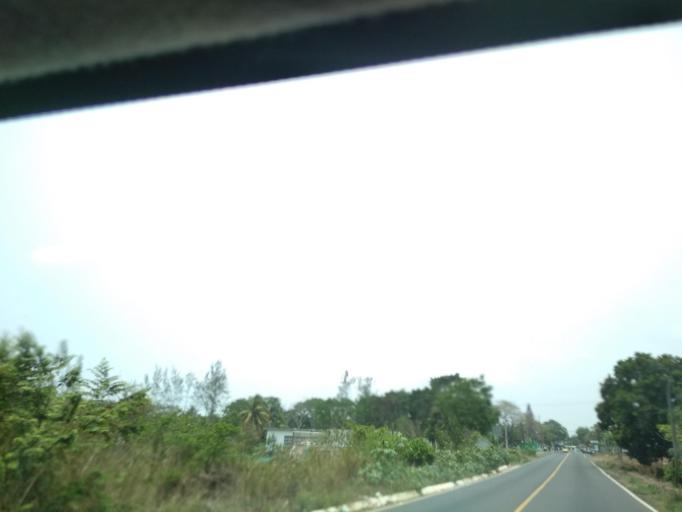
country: MX
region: Veracruz
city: Manlio Fabio Altamirano
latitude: 19.1363
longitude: -96.2986
